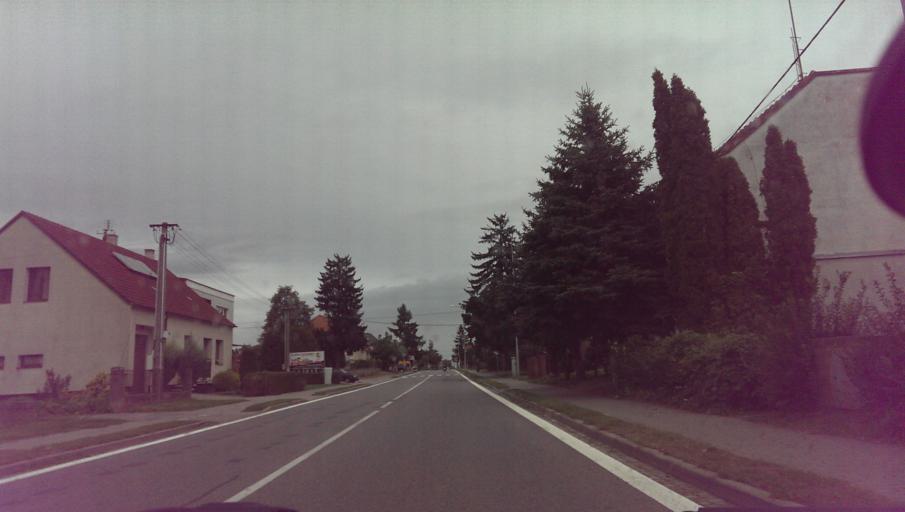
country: CZ
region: South Moravian
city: Bzenec
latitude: 48.9716
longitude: 17.2853
